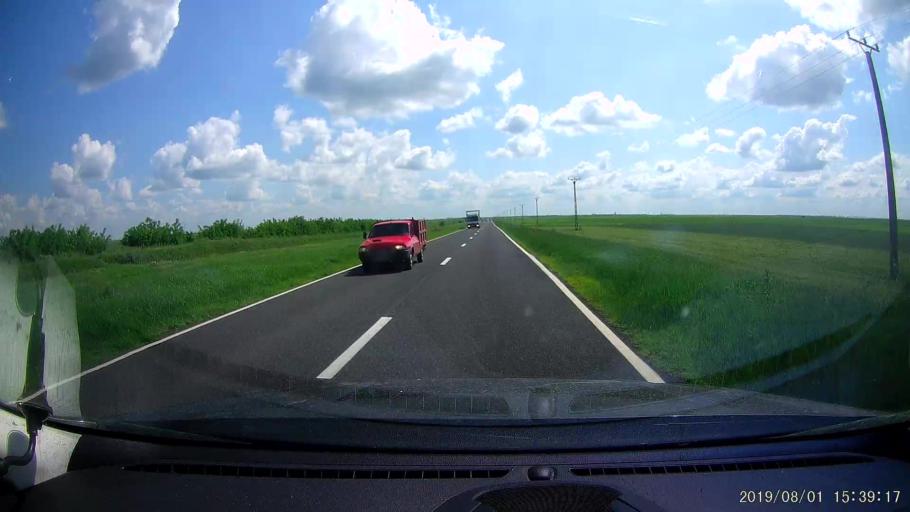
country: RO
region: Braila
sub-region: Comuna Insuratei
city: Insuratei
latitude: 44.8610
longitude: 27.5626
